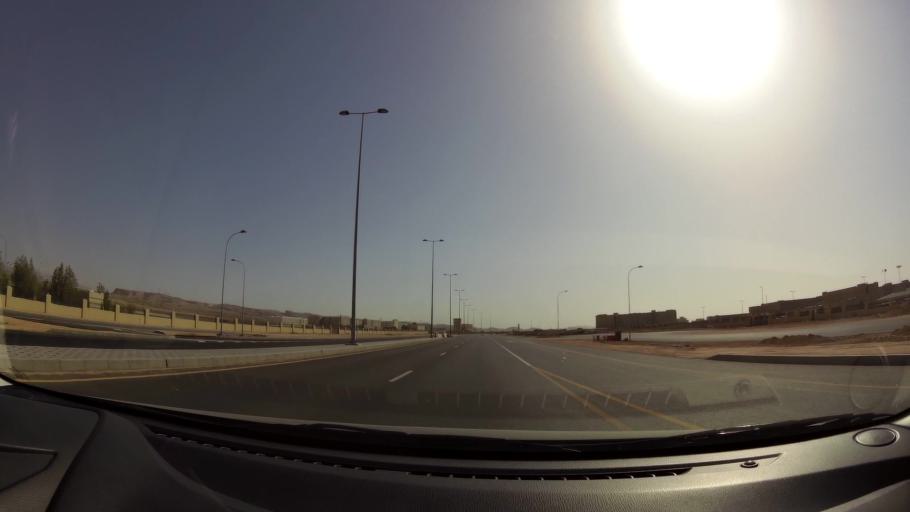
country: OM
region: Muhafazat Masqat
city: Bawshar
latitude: 23.5748
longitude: 58.2892
